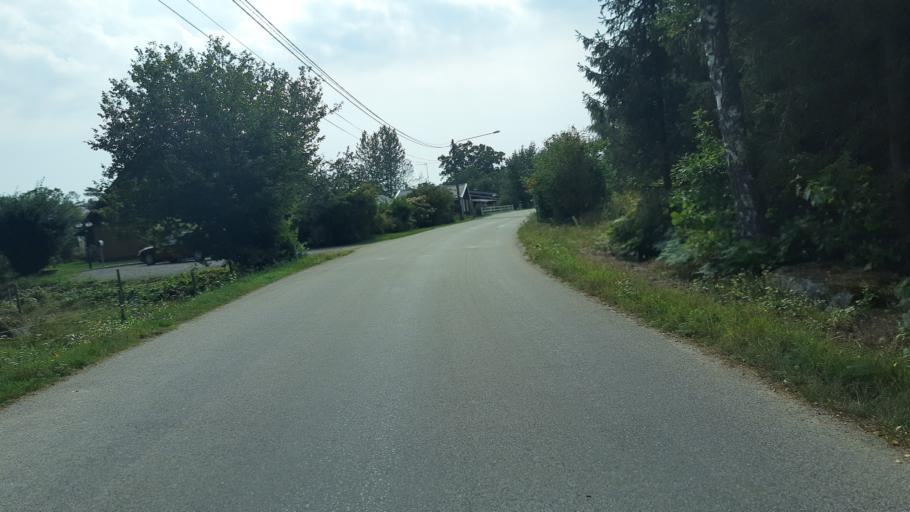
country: SE
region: Blekinge
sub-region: Karlskrona Kommun
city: Nattraby
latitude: 56.1827
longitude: 15.4986
